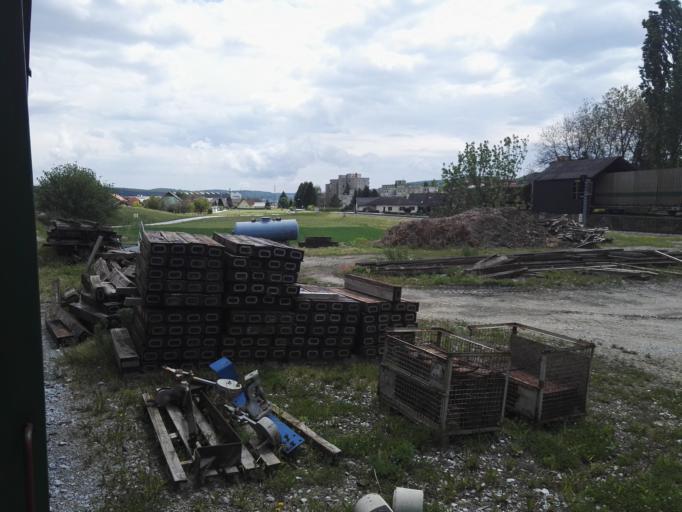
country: AT
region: Styria
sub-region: Politischer Bezirk Weiz
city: Krottendorf
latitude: 47.2126
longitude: 15.6338
